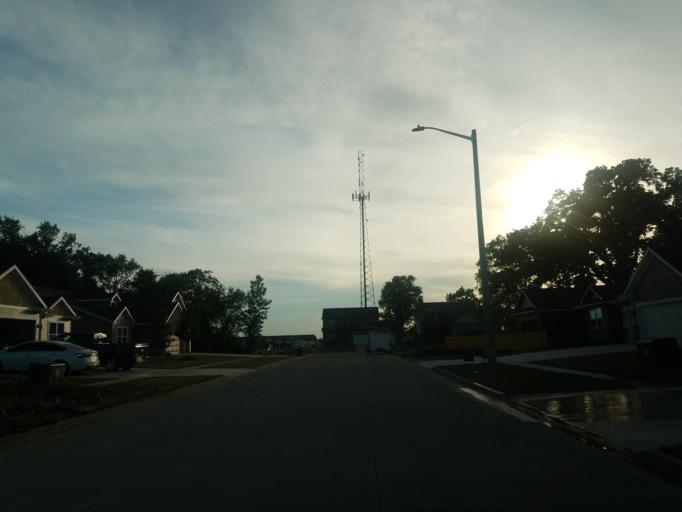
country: US
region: Illinois
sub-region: McLean County
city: Bloomington
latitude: 40.4467
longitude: -89.0087
